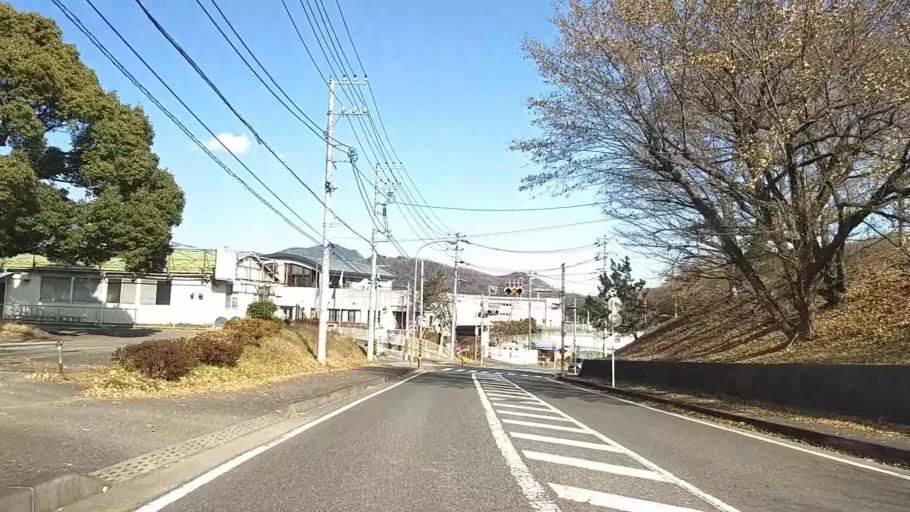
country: JP
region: Kanagawa
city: Hadano
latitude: 35.3557
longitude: 139.2334
